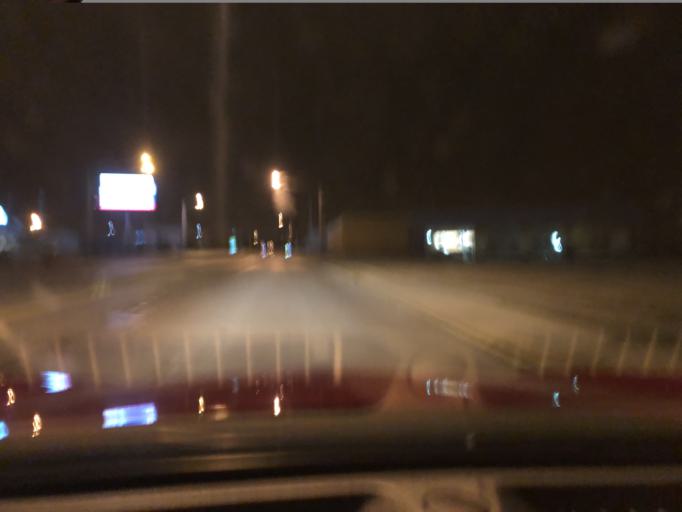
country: US
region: Ohio
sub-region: Logan County
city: Bellefontaine
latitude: 40.3467
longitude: -83.7613
